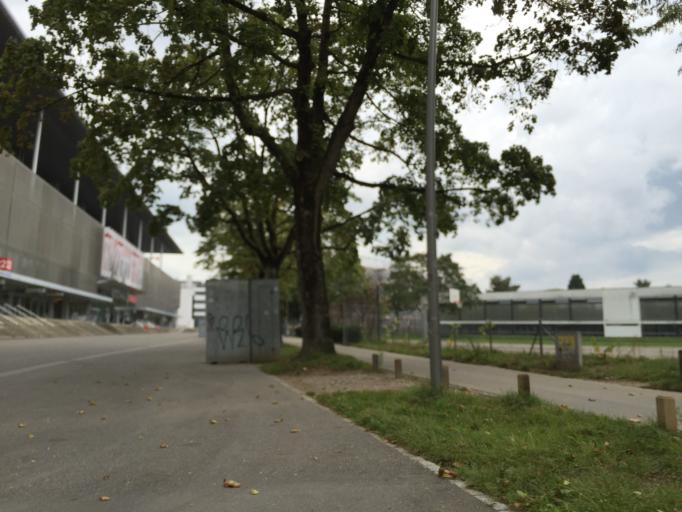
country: CH
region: Bern
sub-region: Bern-Mittelland District
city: Bern
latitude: 46.9646
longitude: 7.4641
